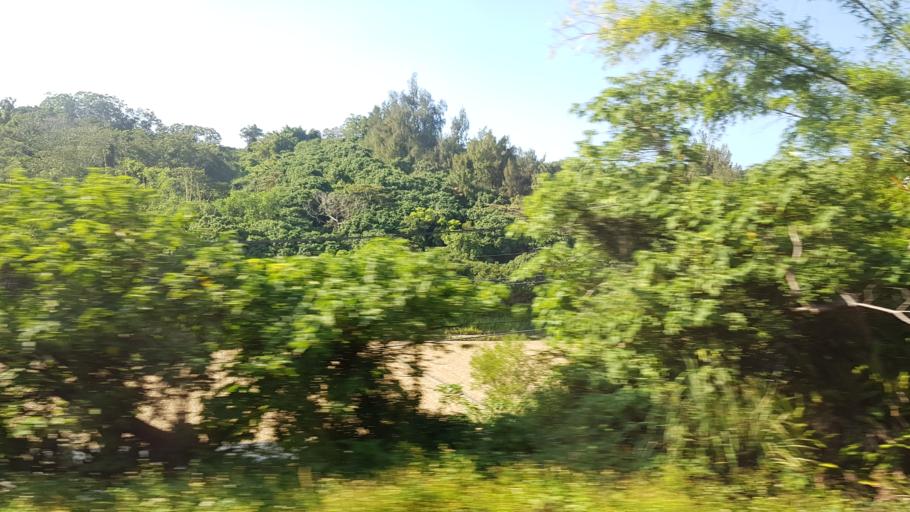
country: TW
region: Taiwan
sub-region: Miaoli
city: Miaoli
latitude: 24.6364
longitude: 120.8621
